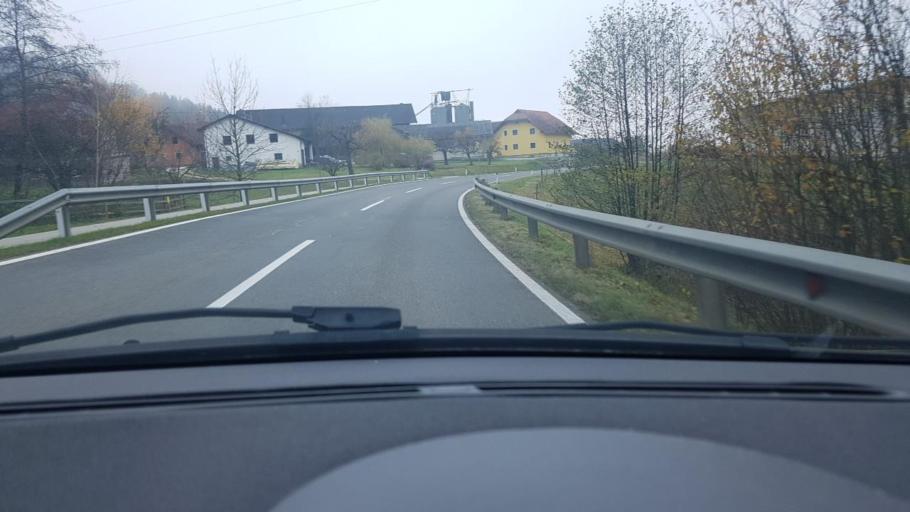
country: AT
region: Carinthia
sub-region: Politischer Bezirk Volkermarkt
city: Neuhaus
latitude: 46.6423
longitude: 14.8614
